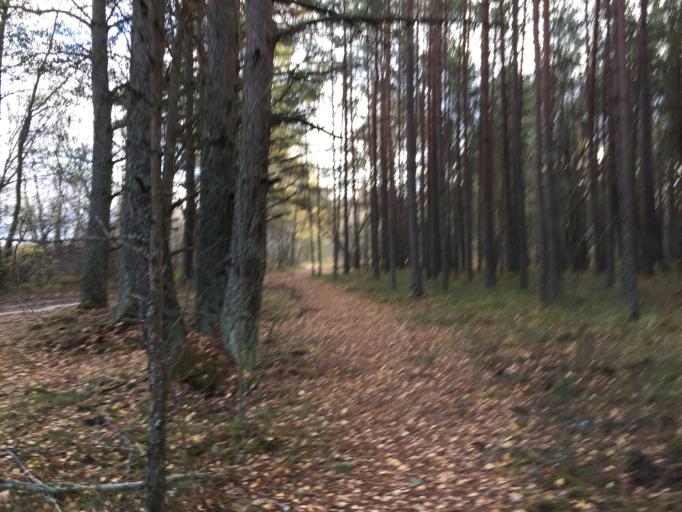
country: LV
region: Carnikava
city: Carnikava
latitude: 57.1511
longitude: 24.2599
